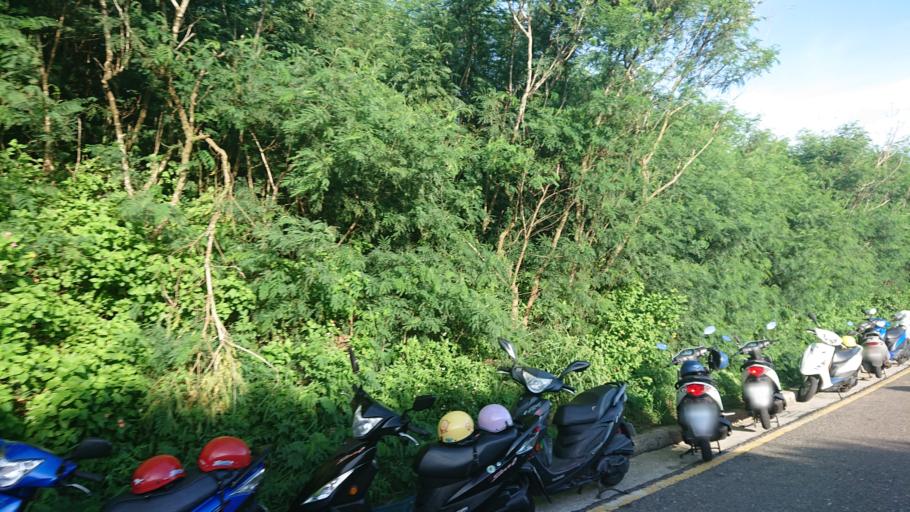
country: TW
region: Taiwan
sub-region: Penghu
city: Ma-kung
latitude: 23.5958
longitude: 119.5165
